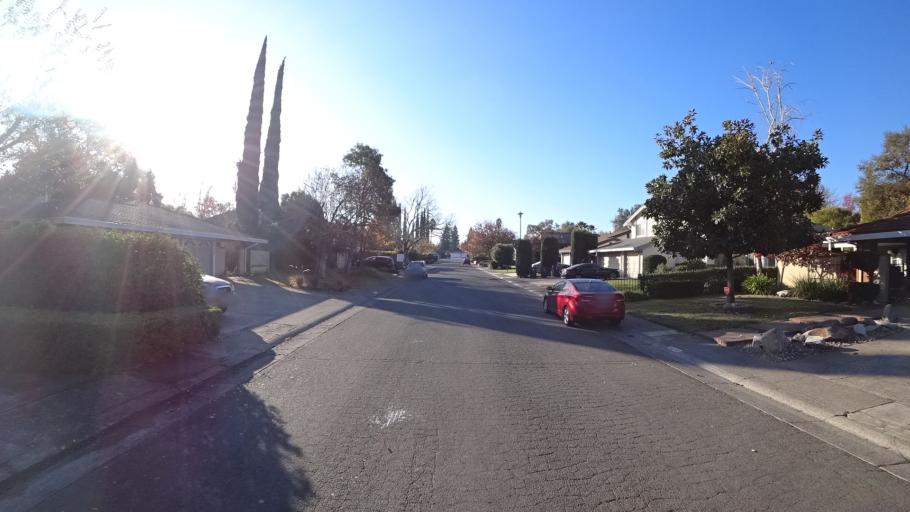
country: US
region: California
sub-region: Sacramento County
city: Citrus Heights
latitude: 38.7166
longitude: -121.2532
